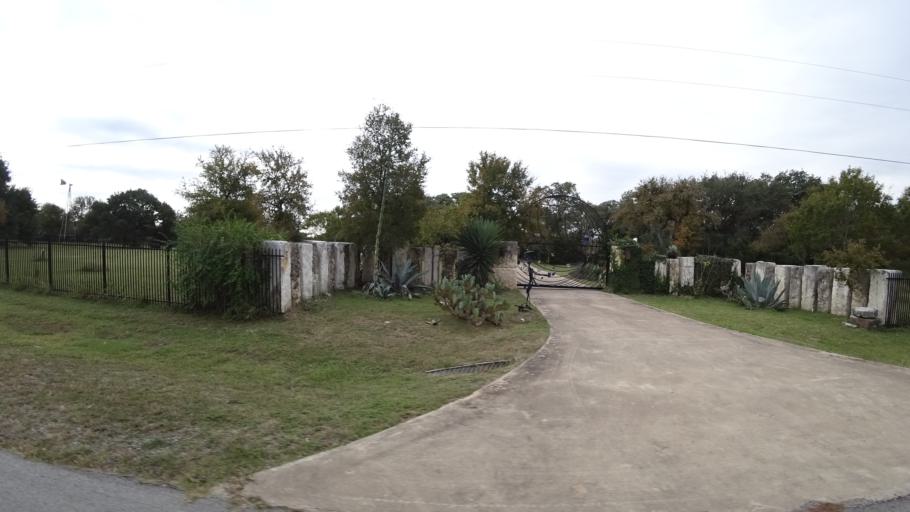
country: US
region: Texas
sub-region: Travis County
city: Shady Hollow
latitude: 30.1482
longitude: -97.8791
